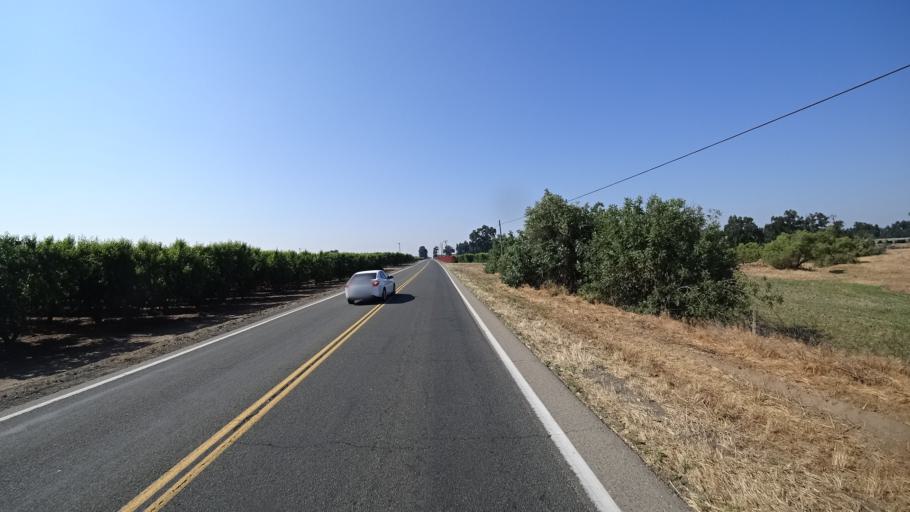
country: US
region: California
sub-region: Fresno County
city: Kingsburg
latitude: 36.4457
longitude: -119.5647
